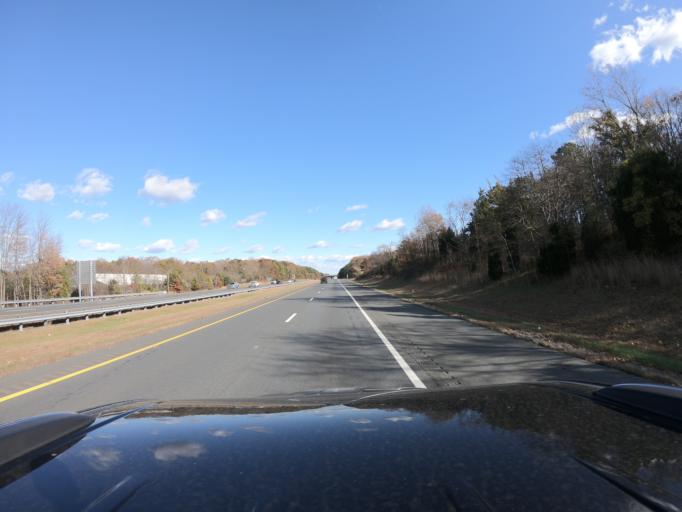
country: US
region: New Jersey
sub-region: Monmouth County
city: Farmingdale
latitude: 40.1667
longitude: -74.2187
